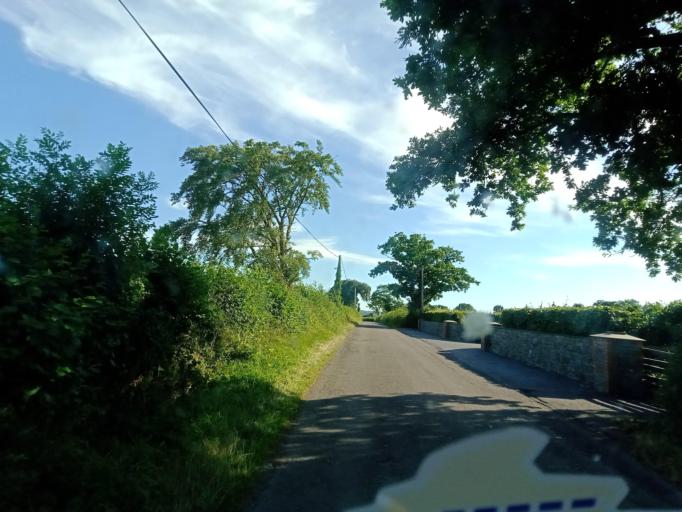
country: IE
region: Leinster
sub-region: Kilkenny
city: Ballyragget
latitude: 52.7609
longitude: -7.3909
